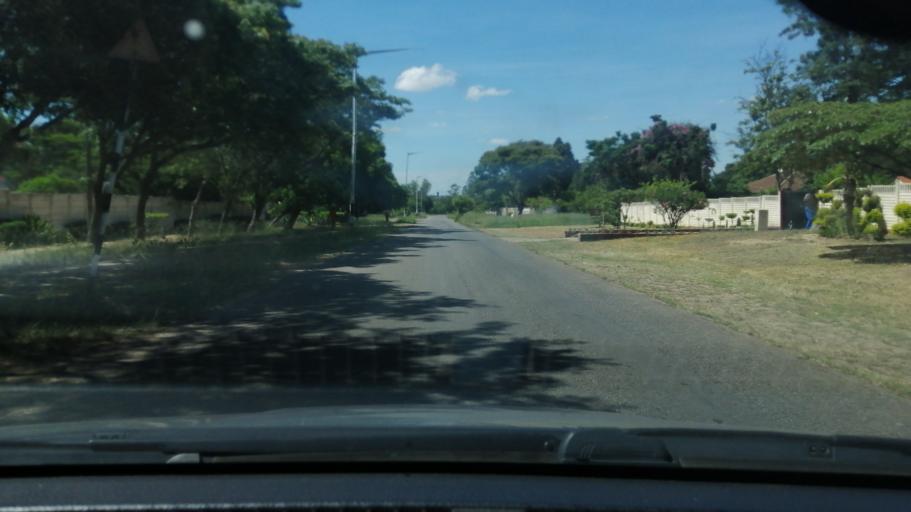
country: ZW
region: Harare
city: Epworth
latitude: -17.8282
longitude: 31.1251
